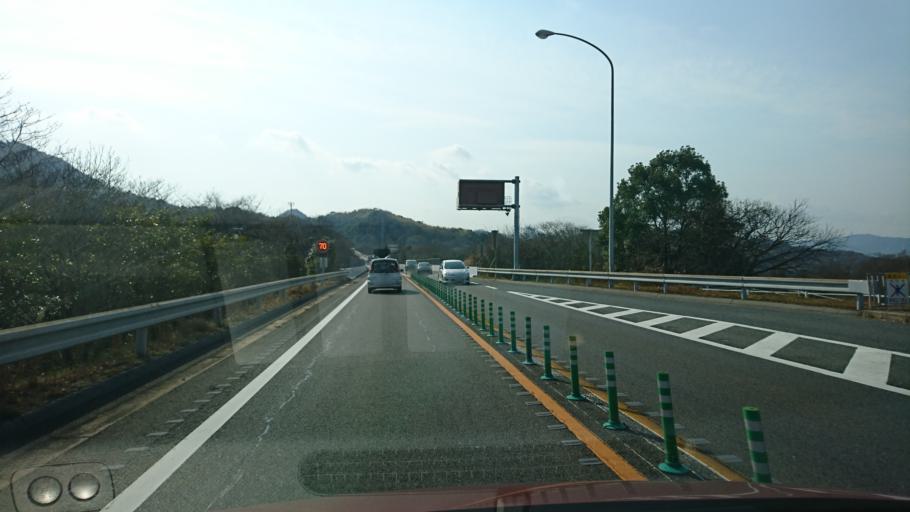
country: JP
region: Hiroshima
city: Onomichi
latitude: 34.3771
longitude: 133.1918
